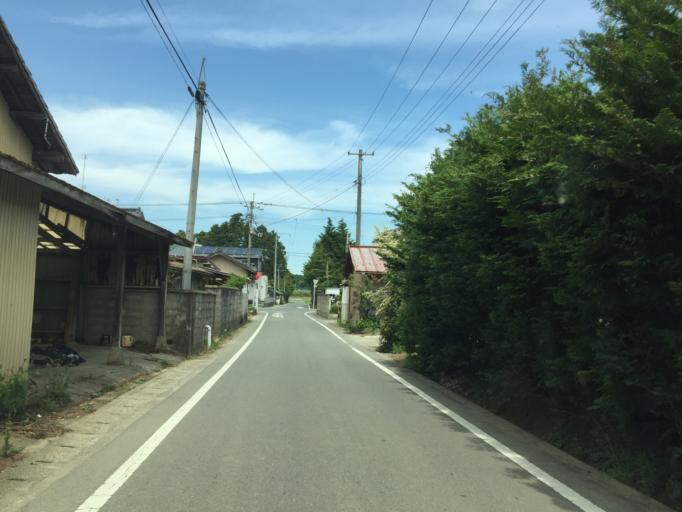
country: JP
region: Miyagi
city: Marumori
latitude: 37.7637
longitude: 140.9351
